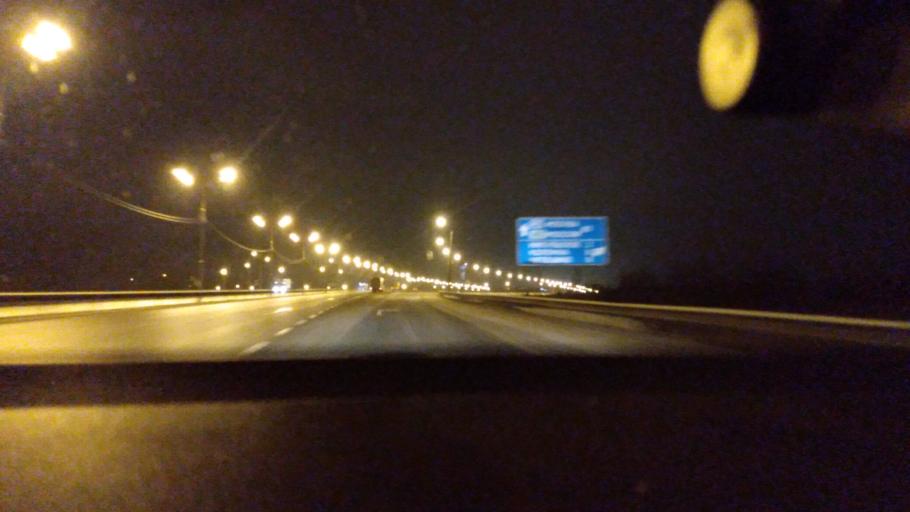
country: RU
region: Moskovskaya
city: Raduzhnyy
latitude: 55.1531
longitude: 38.6999
